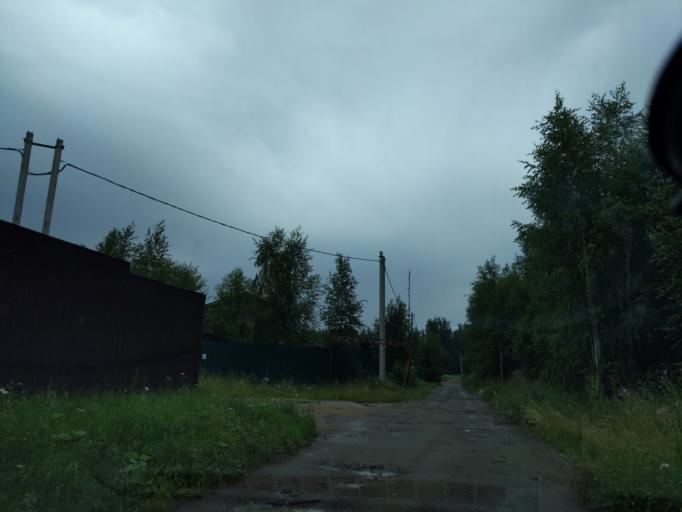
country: RU
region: Moskovskaya
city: Lugovaya
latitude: 56.0547
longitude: 37.4985
